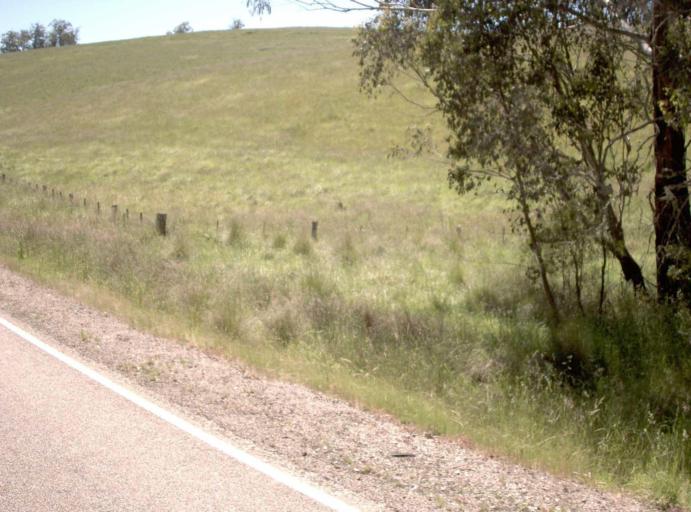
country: AU
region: Victoria
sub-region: East Gippsland
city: Lakes Entrance
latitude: -37.2317
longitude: 148.2606
